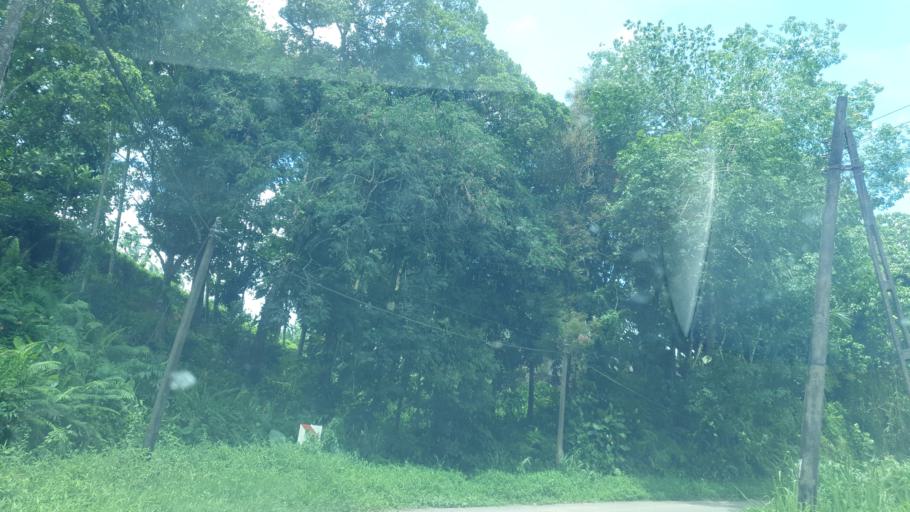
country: LK
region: Sabaragamuwa
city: Ratnapura
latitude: 6.4742
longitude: 80.4203
